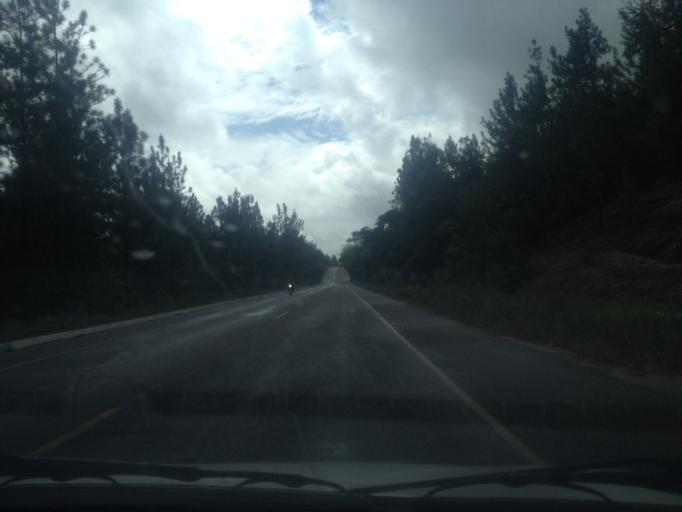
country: BR
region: Bahia
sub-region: Entre Rios
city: Entre Rios
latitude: -12.1184
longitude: -37.7877
